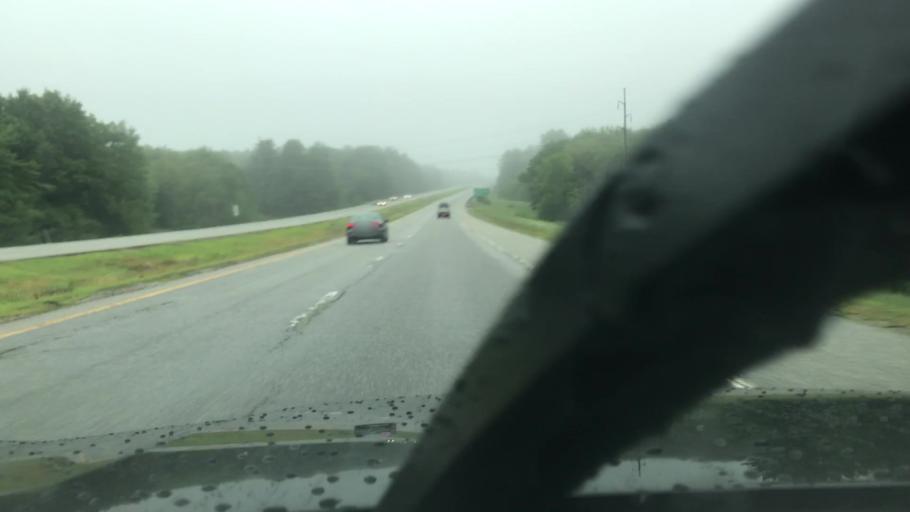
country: US
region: Maine
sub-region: Cumberland County
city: South Portland Gardens
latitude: 43.6088
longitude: -70.3198
